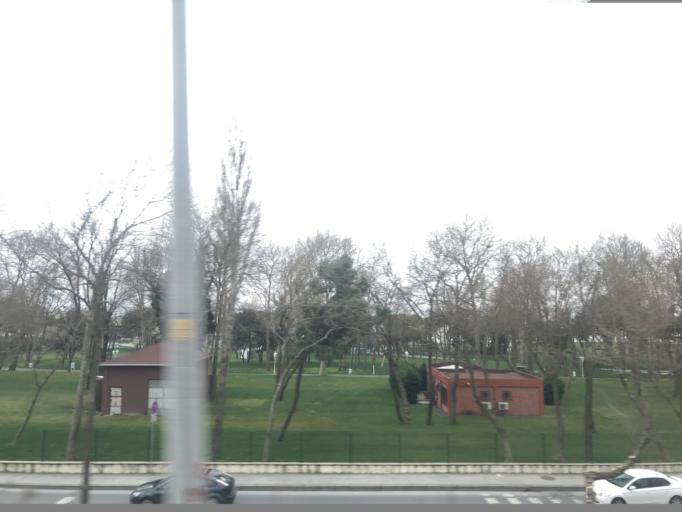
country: TR
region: Istanbul
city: Bahcelievler
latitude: 40.9643
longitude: 28.8043
